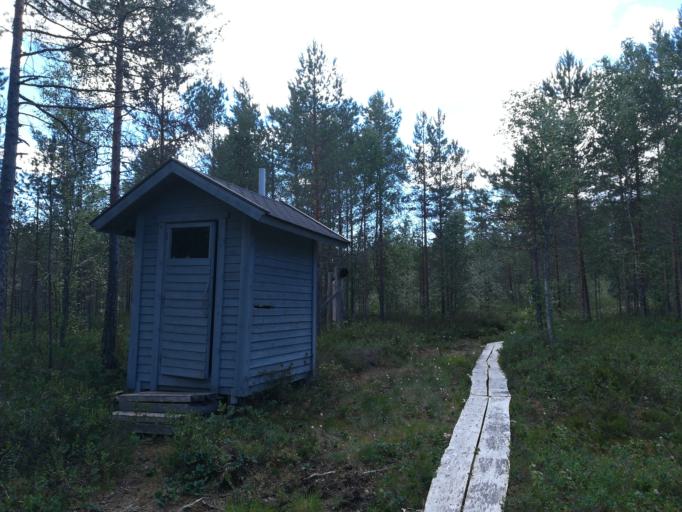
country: FI
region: Southern Savonia
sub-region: Mikkeli
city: Hirvensalmi
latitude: 61.6565
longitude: 26.7785
